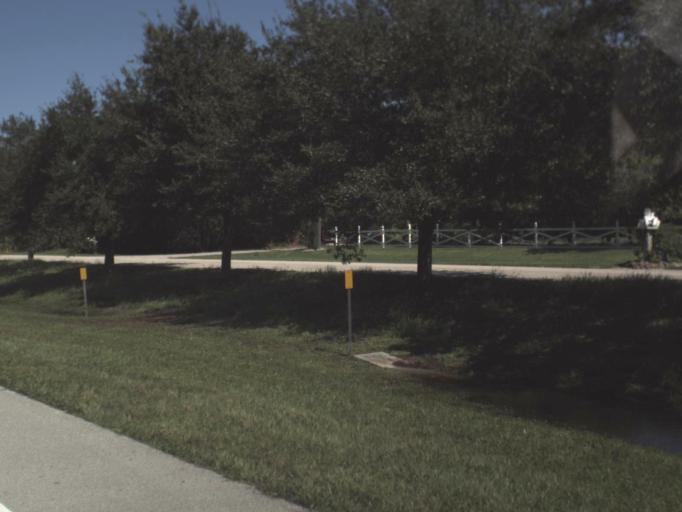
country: US
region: Florida
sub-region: Collier County
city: Pelican Bay
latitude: 26.2396
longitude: -81.8008
